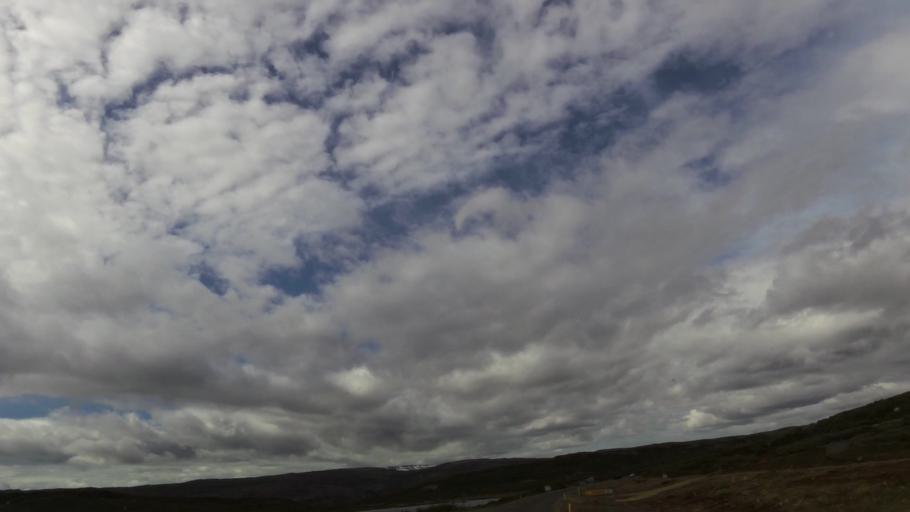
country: IS
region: West
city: Stykkisholmur
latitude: 65.5474
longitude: -22.0983
